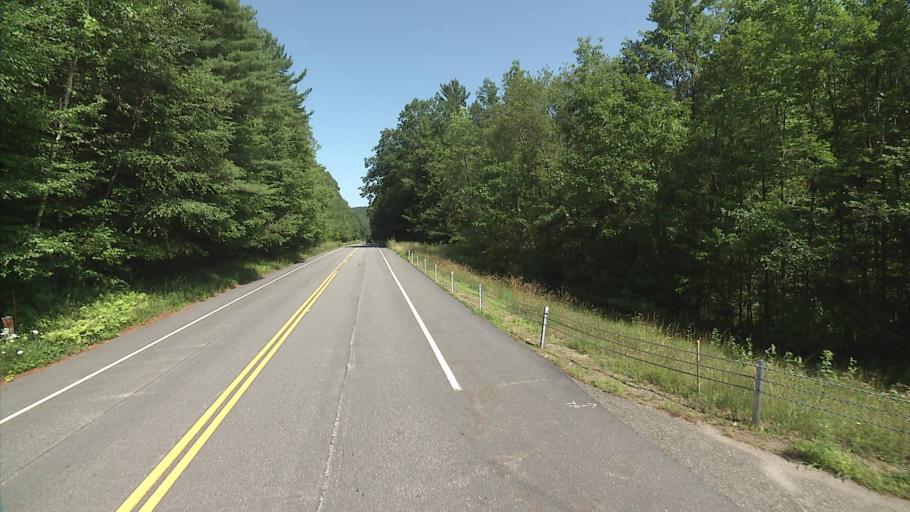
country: US
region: Connecticut
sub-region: Litchfield County
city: Winchester Center
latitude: 41.8842
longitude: -73.1714
